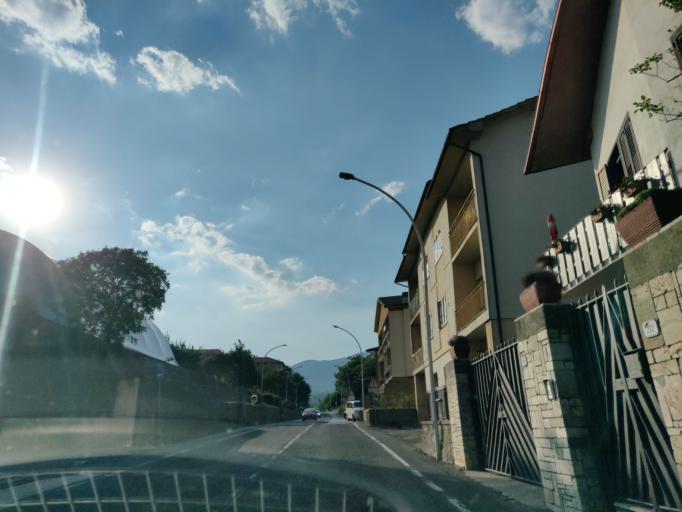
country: IT
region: Tuscany
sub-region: Provincia di Siena
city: Piancastagnaio
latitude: 42.8508
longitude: 11.6903
